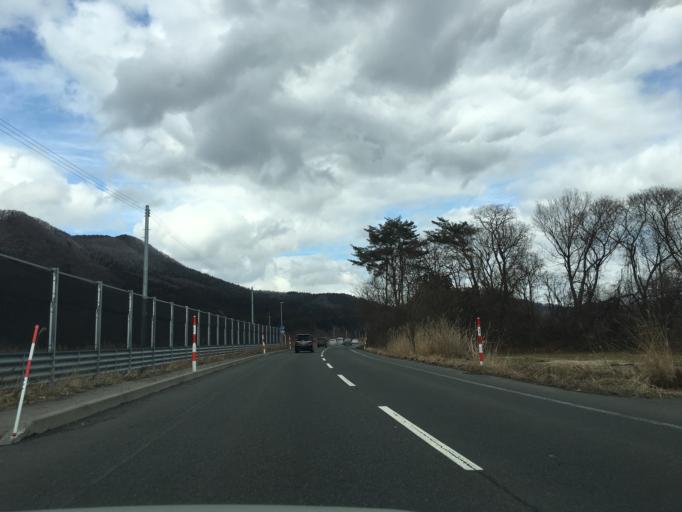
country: JP
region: Akita
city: Hanawa
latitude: 40.2290
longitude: 140.6806
